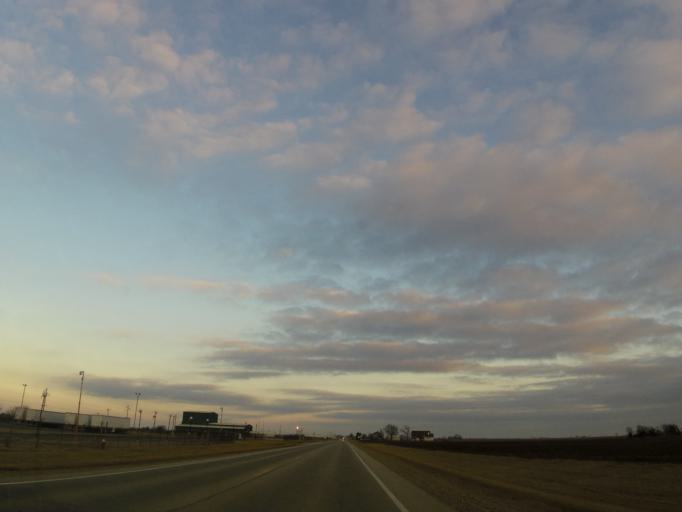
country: US
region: Illinois
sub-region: Woodford County
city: El Paso
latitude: 40.7377
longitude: -88.9946
